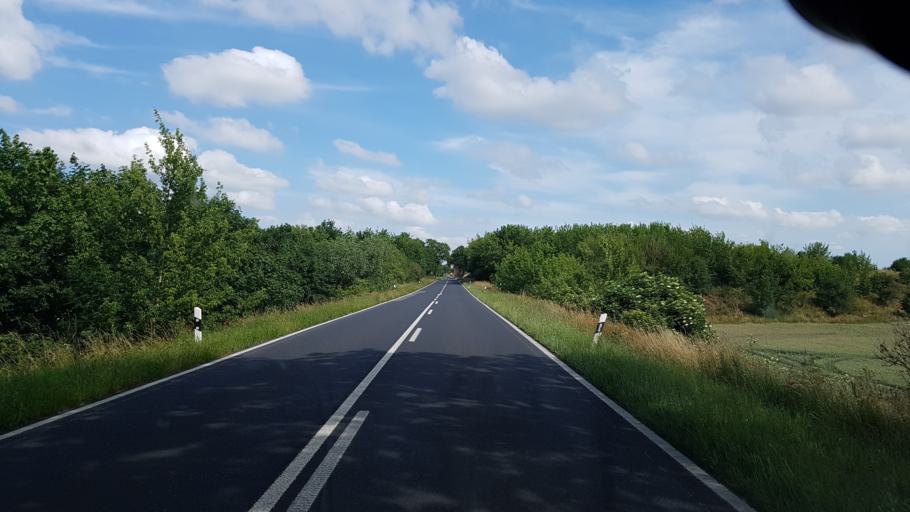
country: DE
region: Brandenburg
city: Prenzlau
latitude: 53.3426
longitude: 13.8244
